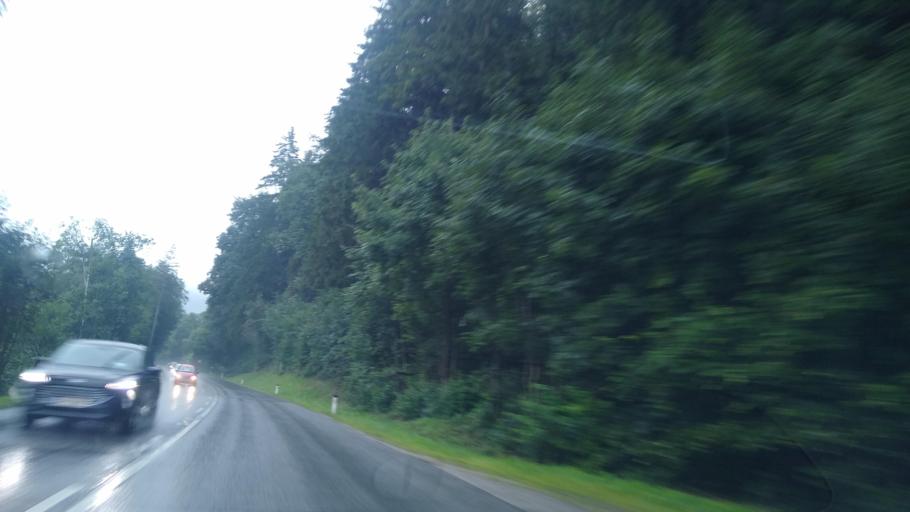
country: AT
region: Tyrol
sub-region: Politischer Bezirk Kufstein
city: Reith im Alpbachtal
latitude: 47.4175
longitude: 11.8600
